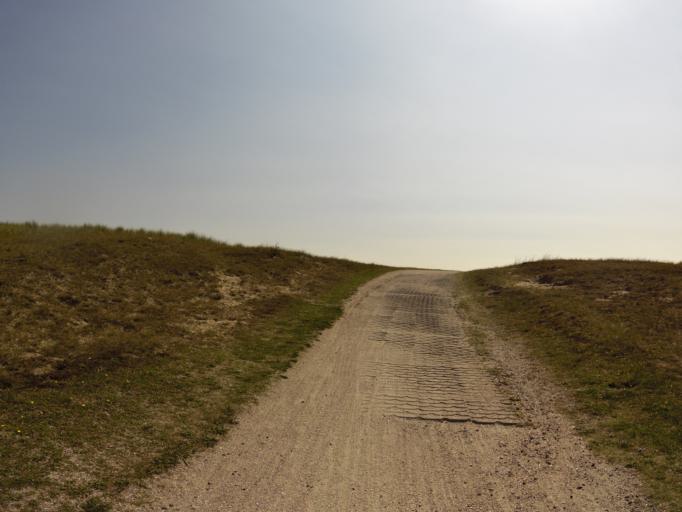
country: NL
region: North Holland
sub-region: Gemeente Schagen
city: Harenkarspel
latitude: 52.7841
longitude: 4.6720
